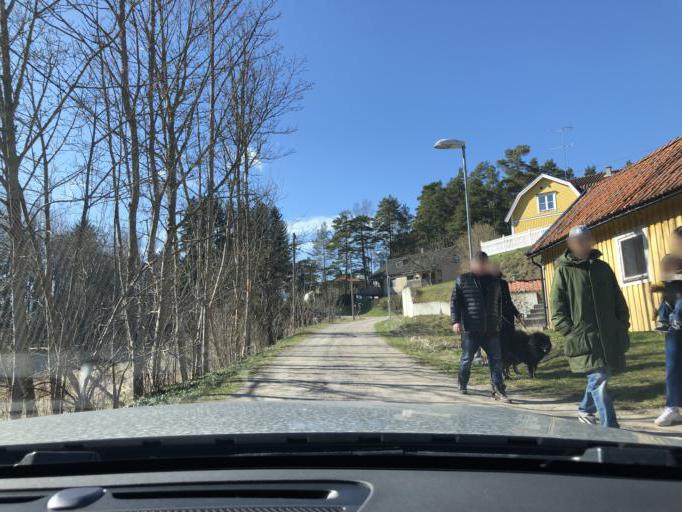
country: SE
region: Soedermanland
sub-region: Trosa Kommun
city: Vagnharad
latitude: 58.9398
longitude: 17.4664
